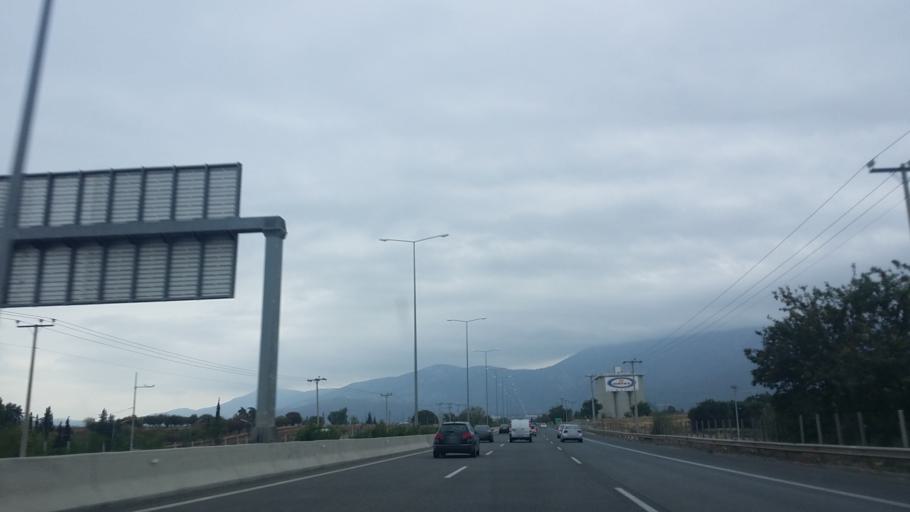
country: GR
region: Attica
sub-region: Nomarchia Anatolikis Attikis
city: Avlonas
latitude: 38.2832
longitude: 23.6826
